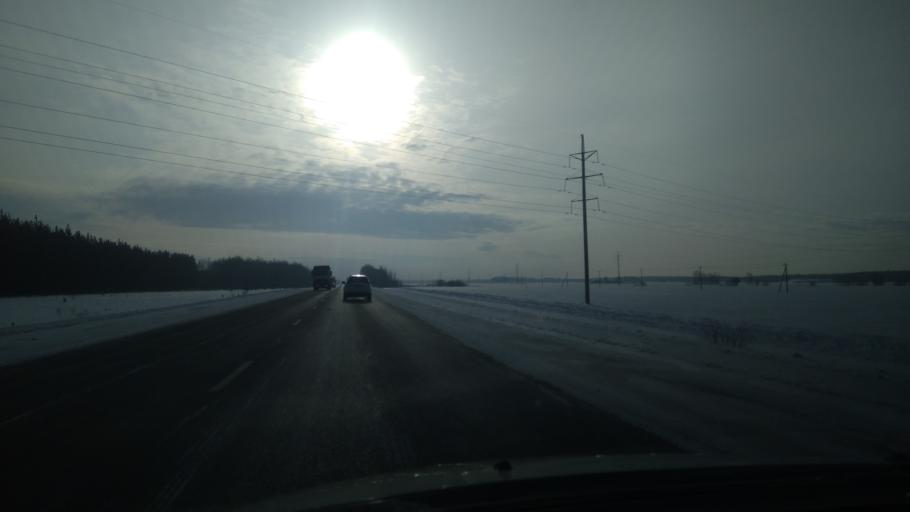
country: RU
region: Sverdlovsk
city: Sukhoy Log
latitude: 56.8643
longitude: 62.0474
